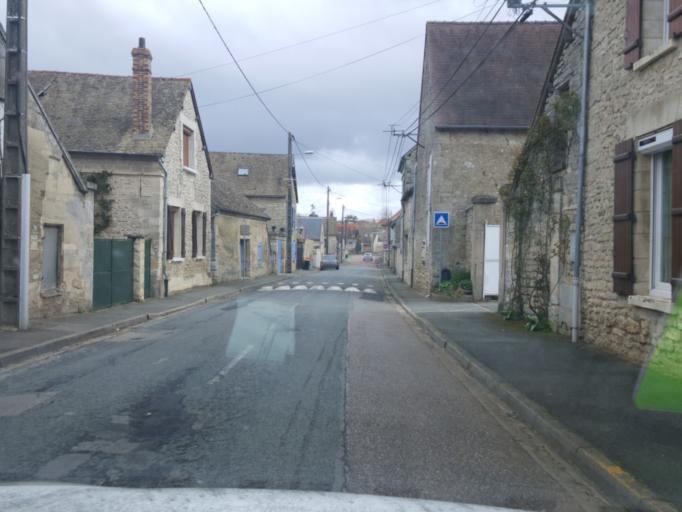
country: FR
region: Ile-de-France
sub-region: Departement du Val-d'Oise
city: Magny-en-Vexin
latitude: 49.1942
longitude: 1.7982
